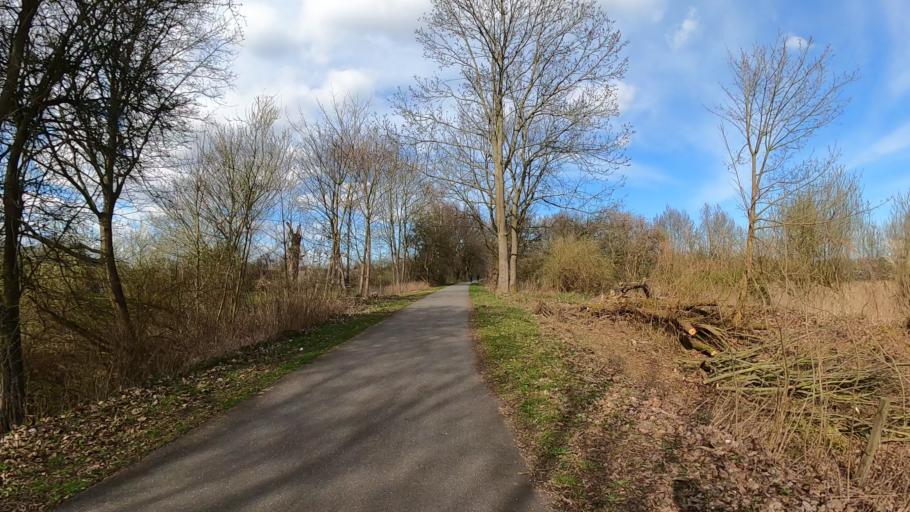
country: DE
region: Hamburg
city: Rothenburgsort
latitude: 53.4906
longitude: 10.0760
